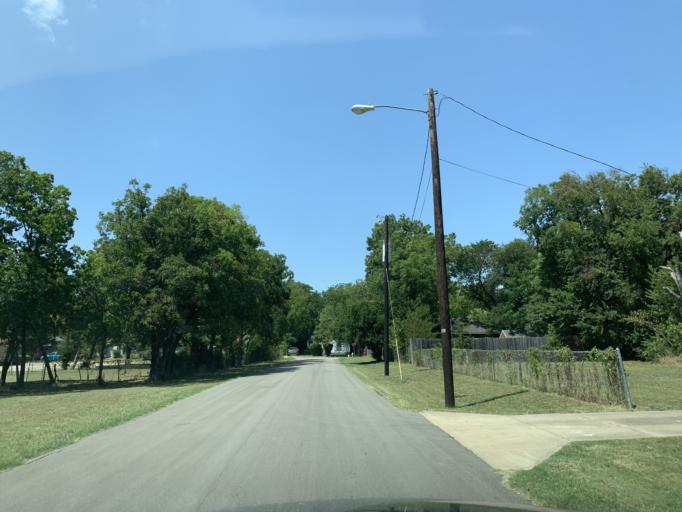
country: US
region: Texas
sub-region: Dallas County
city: Dallas
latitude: 32.6879
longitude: -96.8036
